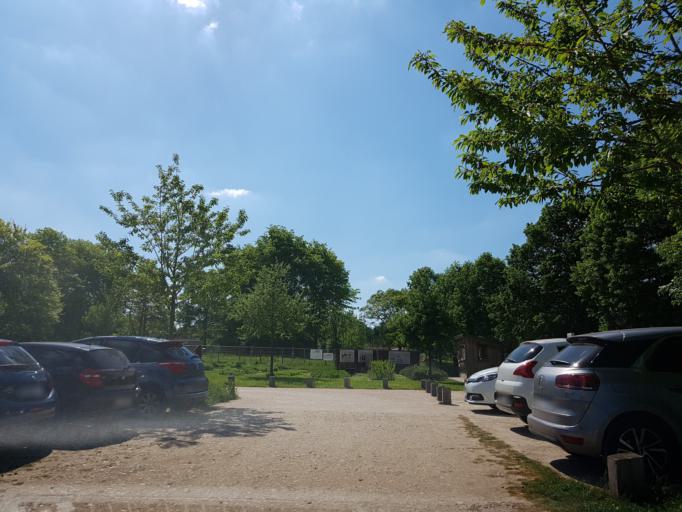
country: FR
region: Ile-de-France
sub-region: Departement des Hauts-de-Seine
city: Chatenay-Malabry
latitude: 48.7706
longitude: 2.2731
